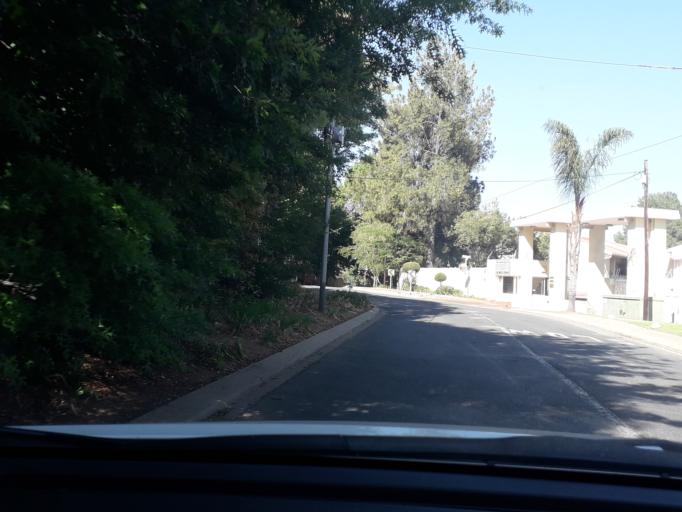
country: ZA
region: Gauteng
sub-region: City of Johannesburg Metropolitan Municipality
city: Johannesburg
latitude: -26.0893
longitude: 28.0507
